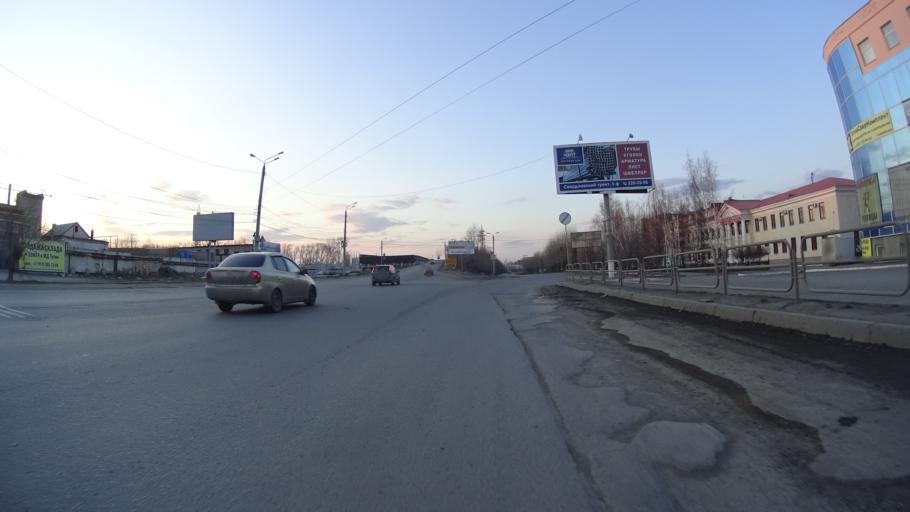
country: RU
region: Chelyabinsk
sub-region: Gorod Chelyabinsk
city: Chelyabinsk
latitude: 55.1130
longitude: 61.3868
